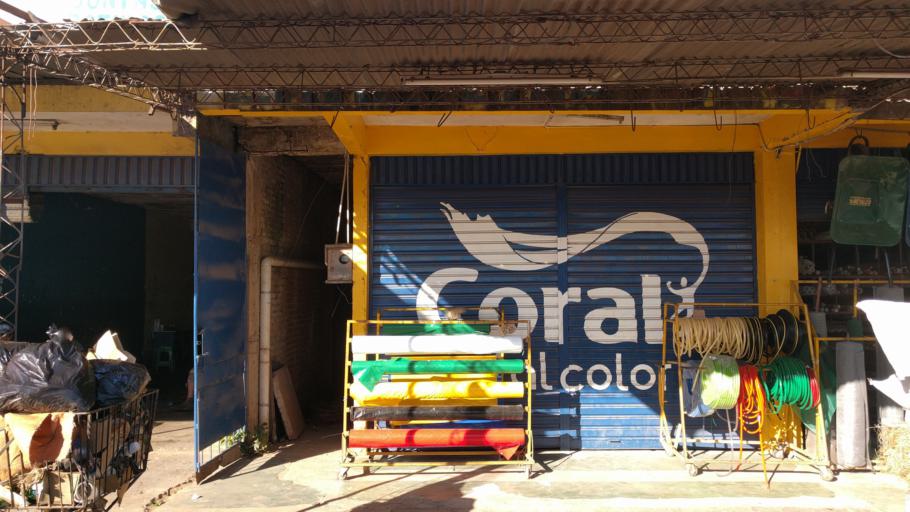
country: BO
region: Santa Cruz
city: Santa Cruz de la Sierra
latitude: -17.7497
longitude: -63.1869
